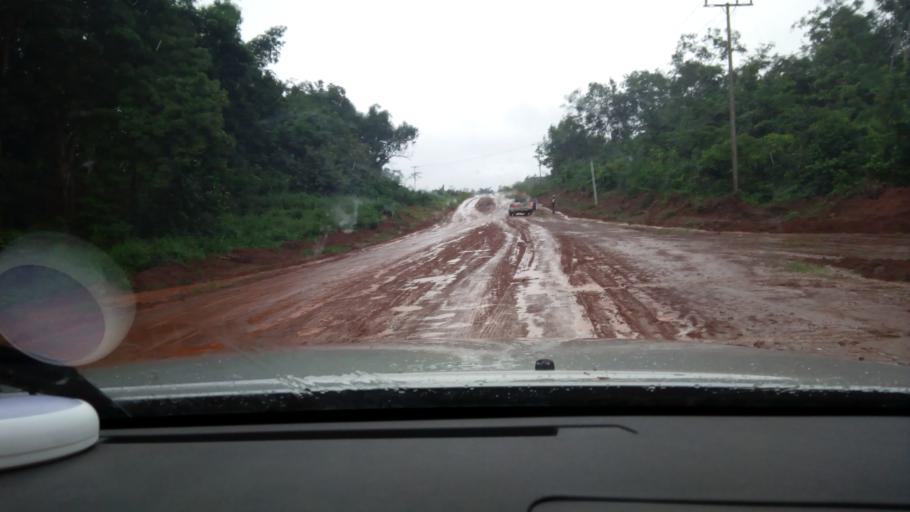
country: LR
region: Nimba
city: Sanniquellie
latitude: 7.0980
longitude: -8.8916
